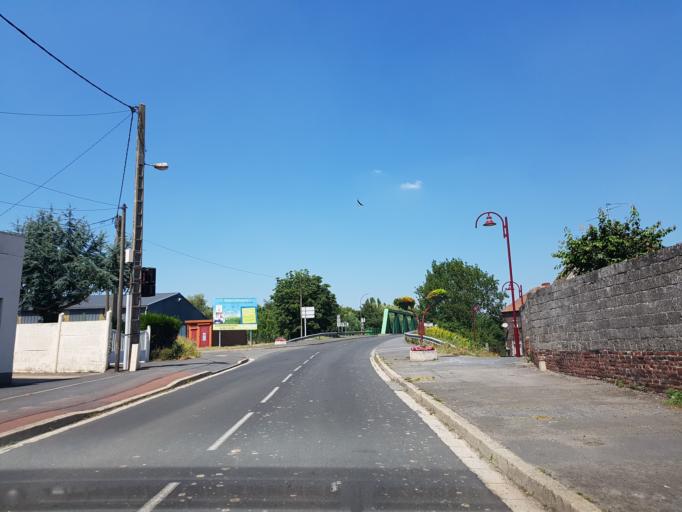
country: FR
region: Nord-Pas-de-Calais
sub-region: Departement du Nord
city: Neuville-sur-Escaut
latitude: 50.3009
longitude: 3.3513
